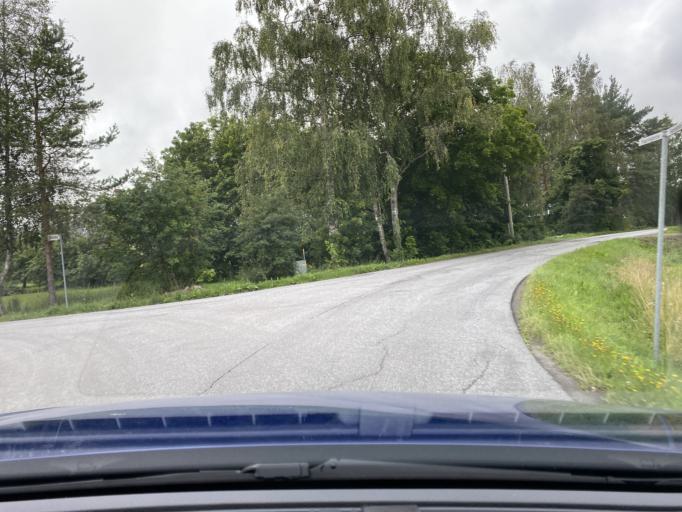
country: FI
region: Ostrobothnia
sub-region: Kyroenmaa
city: Laihia
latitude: 62.9836
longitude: 21.9942
